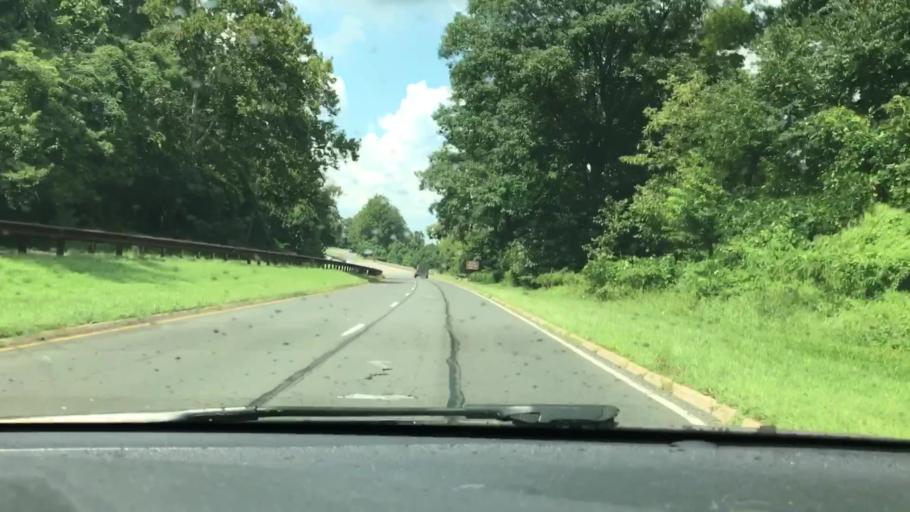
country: US
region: Maryland
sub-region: Montgomery County
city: Brookmont
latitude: 38.9178
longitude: -77.1067
